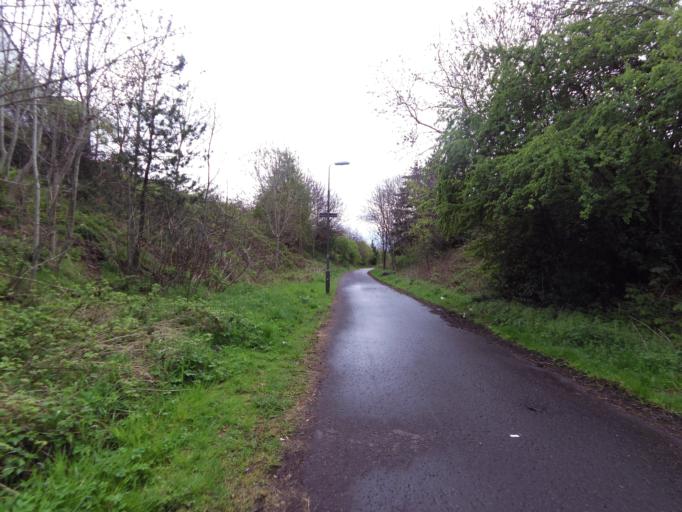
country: GB
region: Scotland
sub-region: Edinburgh
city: Edinburgh
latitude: 55.9605
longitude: -3.2481
